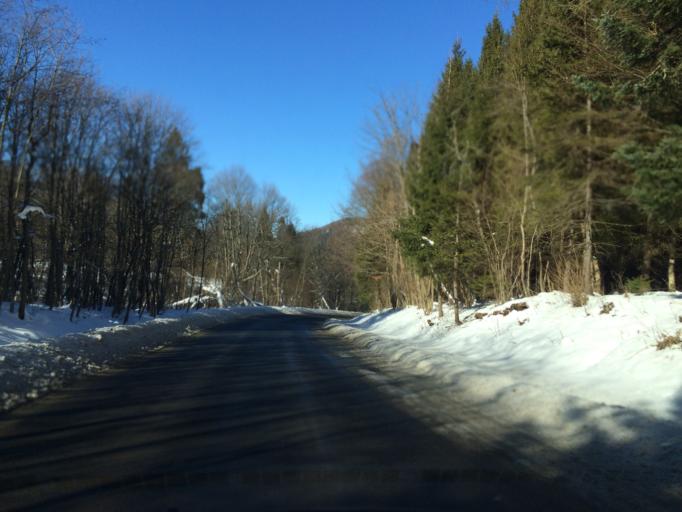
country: PL
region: Subcarpathian Voivodeship
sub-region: Powiat leski
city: Cisna
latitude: 49.1924
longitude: 22.3745
